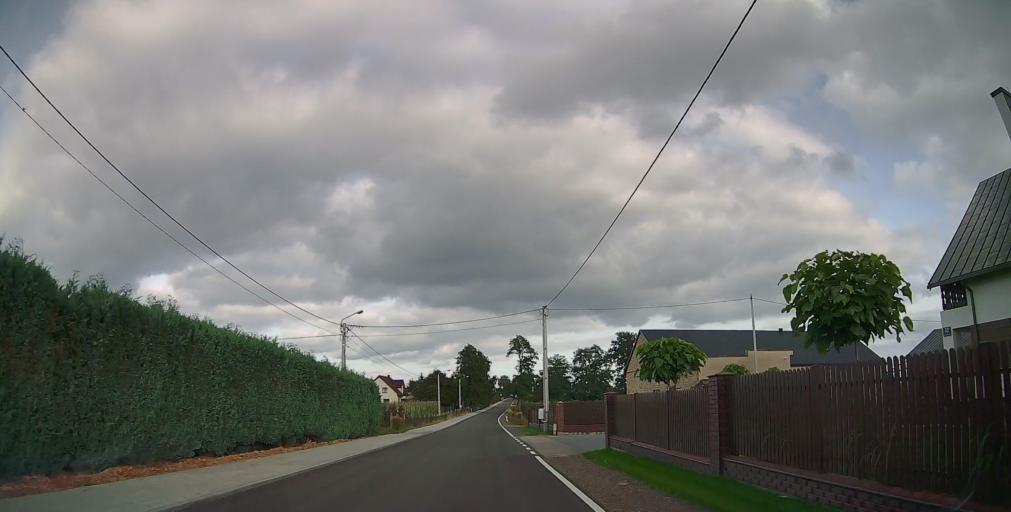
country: PL
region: Masovian Voivodeship
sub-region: Powiat bialobrzeski
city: Promna
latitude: 51.7083
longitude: 20.9333
